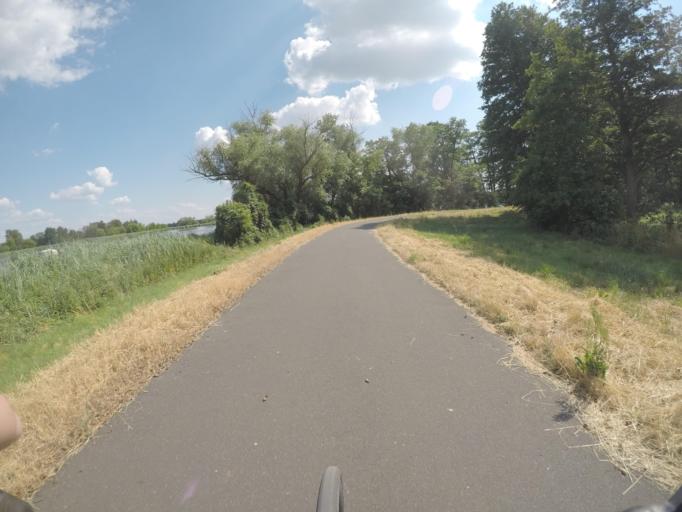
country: DE
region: Brandenburg
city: Ketzin
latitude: 52.4427
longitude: 12.8784
